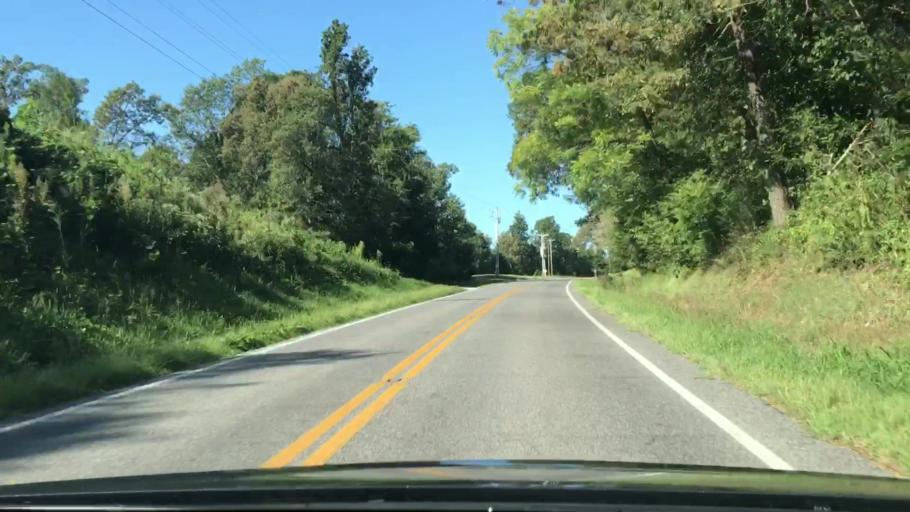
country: US
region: Kentucky
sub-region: Graves County
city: Mayfield
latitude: 36.7669
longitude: -88.5675
